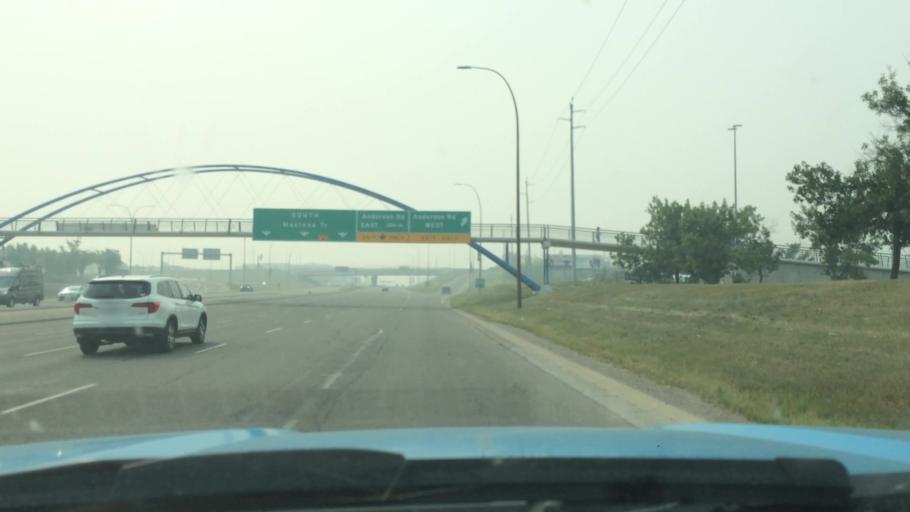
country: CA
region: Alberta
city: Calgary
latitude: 50.9545
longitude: -114.0719
